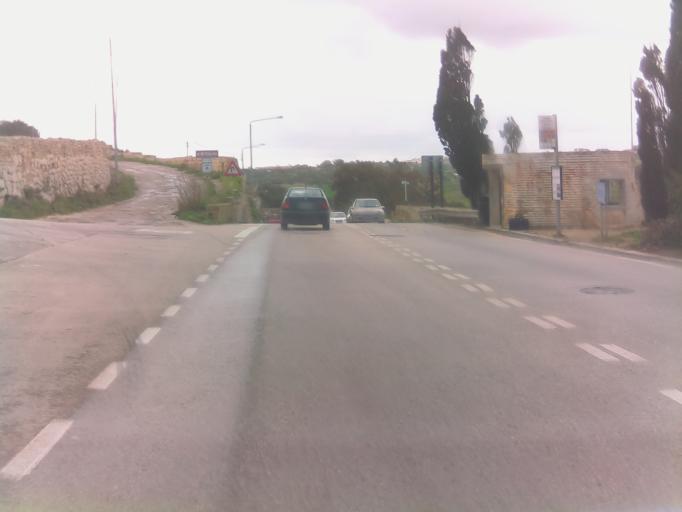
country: MT
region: Il-Mosta
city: Mosta
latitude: 35.9174
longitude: 14.4150
